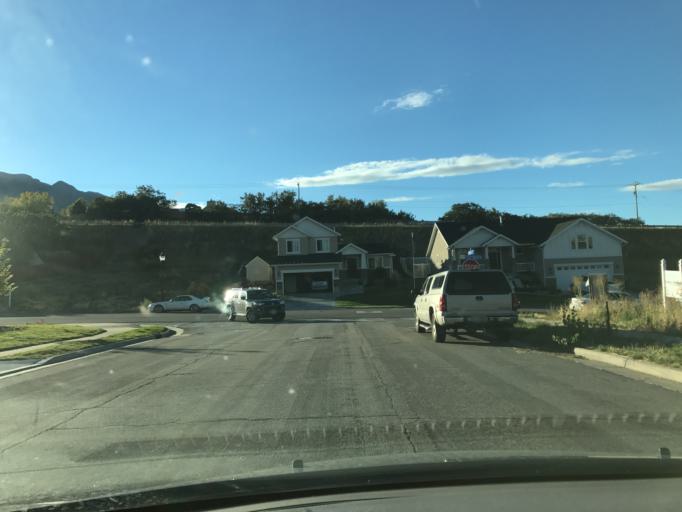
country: US
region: Utah
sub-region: Davis County
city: South Weber
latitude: 41.1051
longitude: -111.9264
